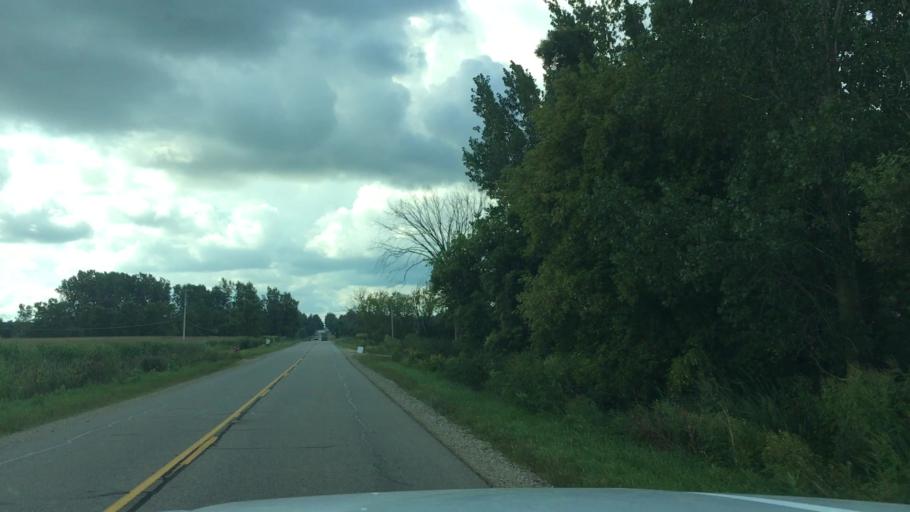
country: US
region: Michigan
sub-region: Ottawa County
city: Hudsonville
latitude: 42.7913
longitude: -85.8418
